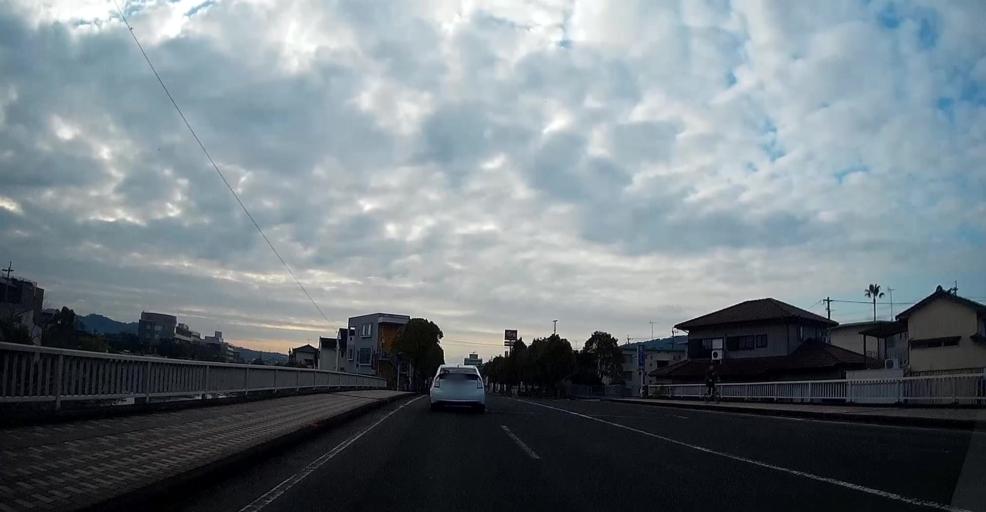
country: JP
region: Kumamoto
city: Hondo
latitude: 32.4628
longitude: 130.1908
